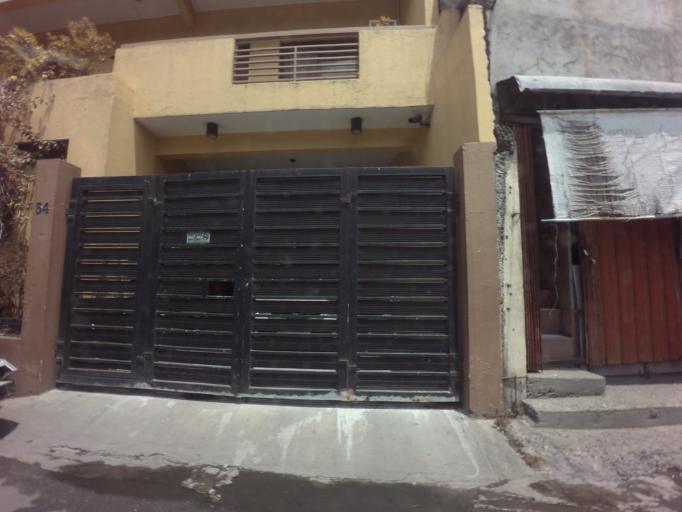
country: PH
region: Calabarzon
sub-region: Province of Laguna
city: San Pedro
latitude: 14.4087
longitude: 121.0500
